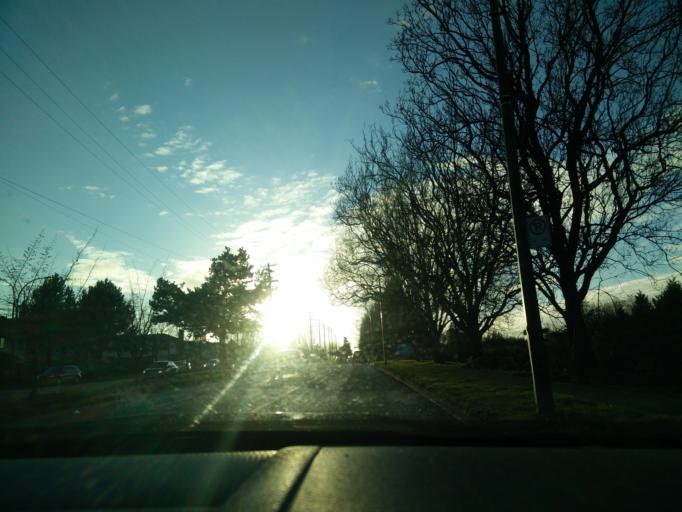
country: CA
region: British Columbia
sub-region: Fraser Valley Regional District
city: North Vancouver
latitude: 49.2697
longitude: -123.0295
